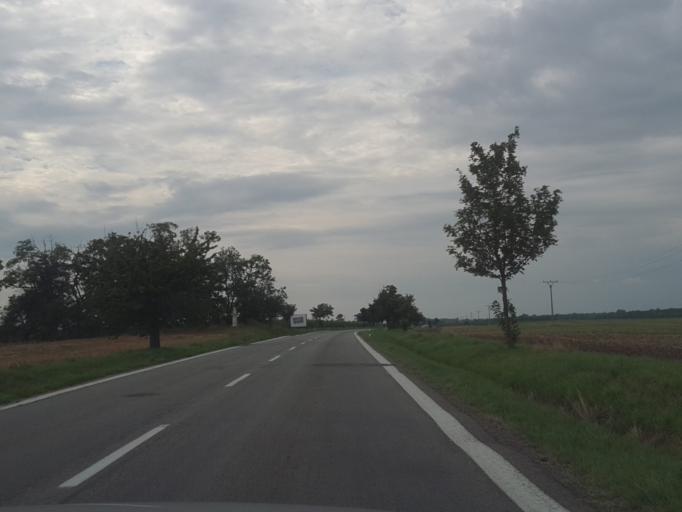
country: SK
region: Nitriansky
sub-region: Okres Nove Zamky
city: Nove Zamky
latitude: 48.0340
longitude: 18.1286
